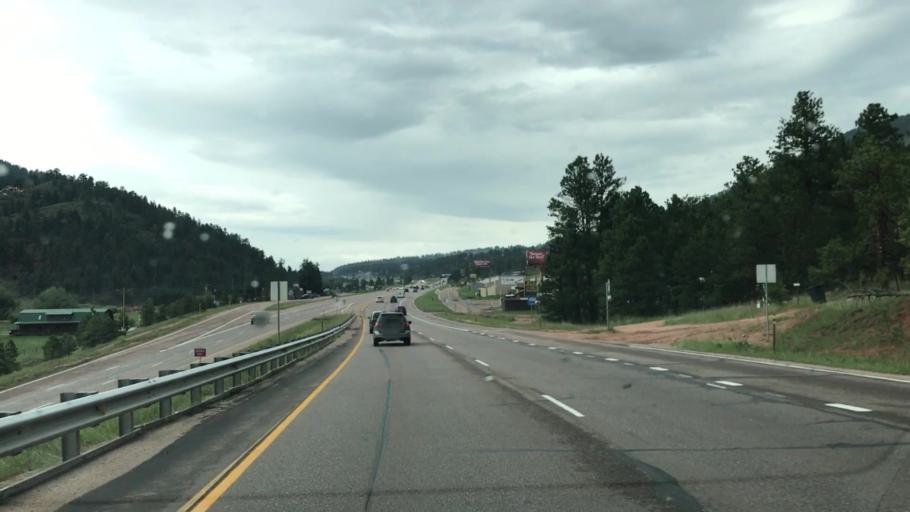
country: US
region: Colorado
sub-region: El Paso County
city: Cascade-Chipita Park
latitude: 38.9528
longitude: -105.0259
